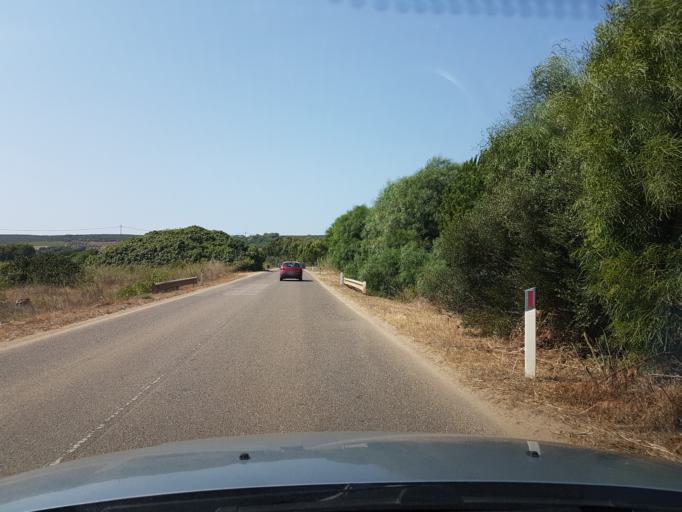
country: IT
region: Sardinia
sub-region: Provincia di Oristano
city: Cabras
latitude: 39.9167
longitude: 8.4519
